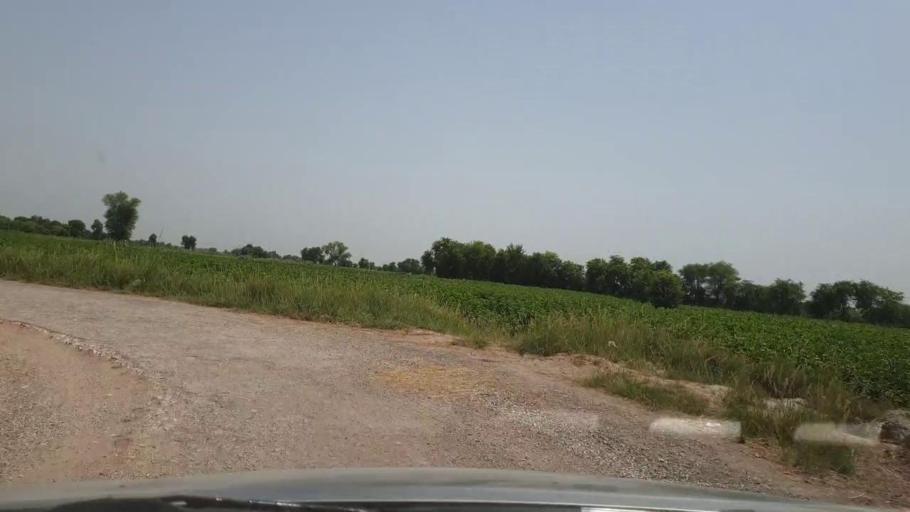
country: PK
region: Sindh
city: Pano Aqil
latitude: 27.7982
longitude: 69.2419
